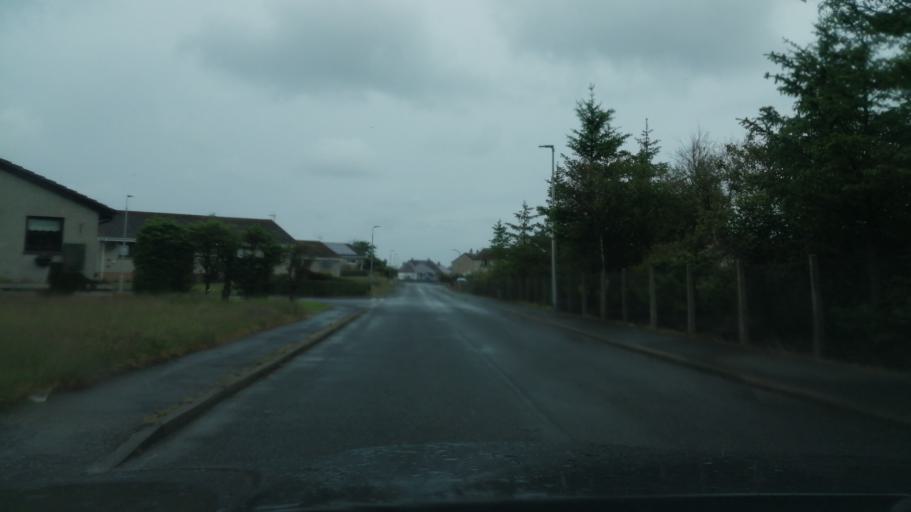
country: GB
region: Scotland
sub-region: Aberdeenshire
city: Portsoy
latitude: 57.6803
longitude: -2.6998
